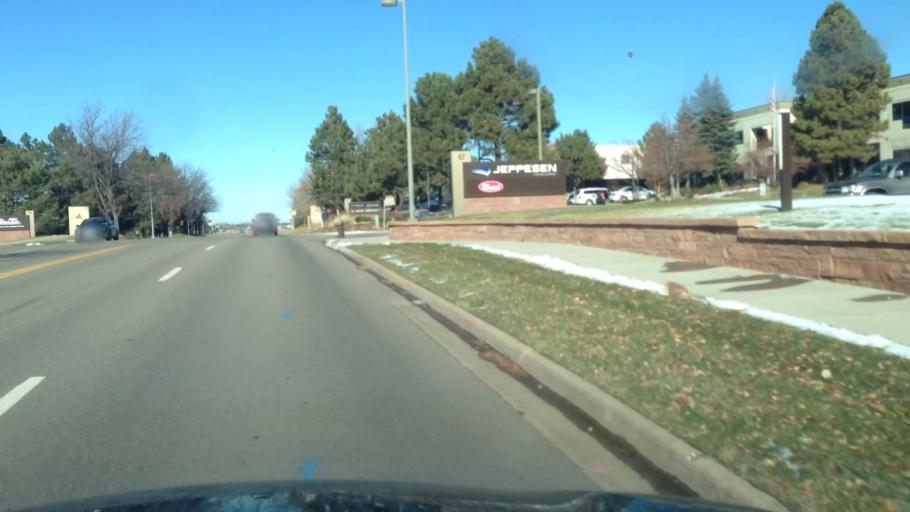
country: US
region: Colorado
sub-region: Arapahoe County
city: Centennial
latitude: 39.5783
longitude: -104.8568
